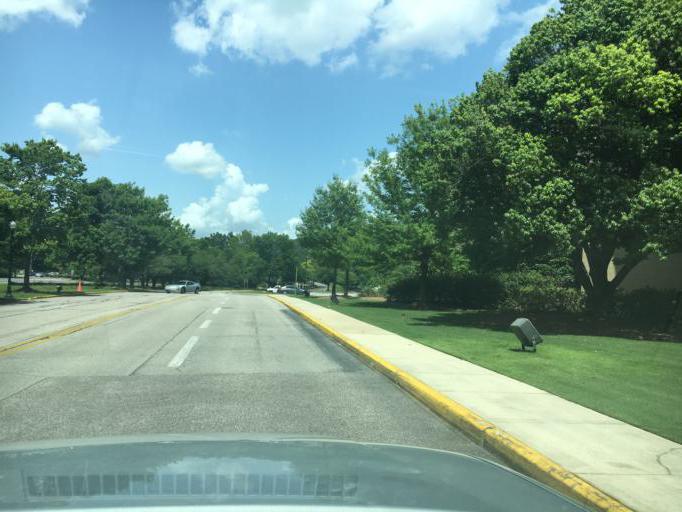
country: US
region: Alabama
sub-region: Jefferson County
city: Vestavia Hills
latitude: 33.4717
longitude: -86.7696
